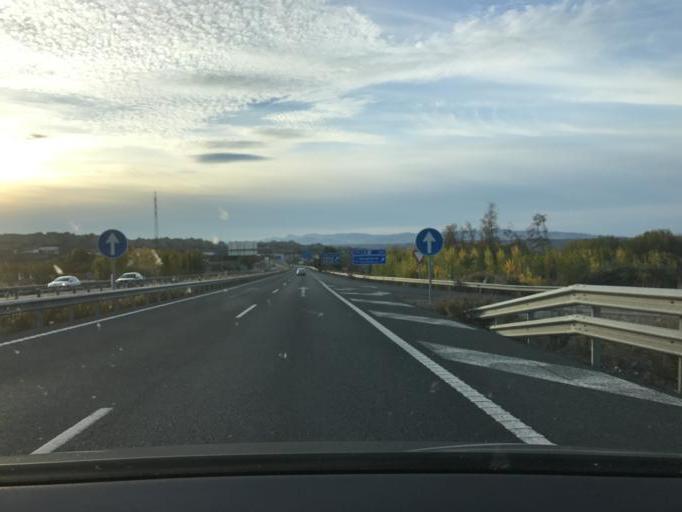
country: ES
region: Andalusia
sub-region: Provincia de Granada
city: Guadix
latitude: 37.3195
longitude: -3.1399
